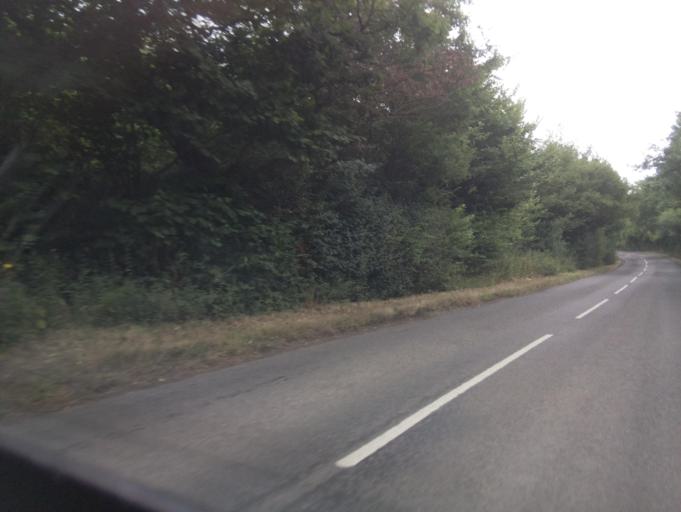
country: GB
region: England
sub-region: Leicestershire
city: Measham
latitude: 52.7261
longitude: -1.5118
